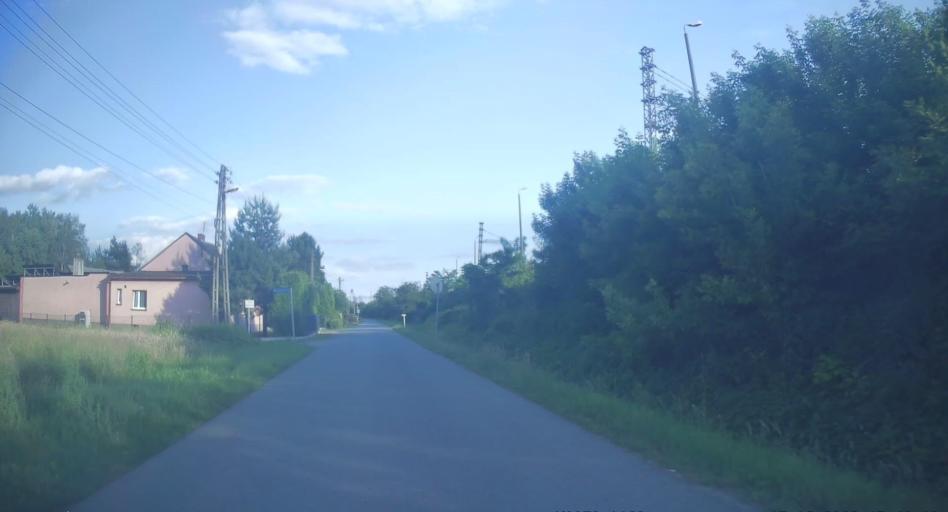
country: PL
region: Lesser Poland Voivodeship
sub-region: Powiat oswiecimski
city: Babice
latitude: 50.0721
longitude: 19.1866
